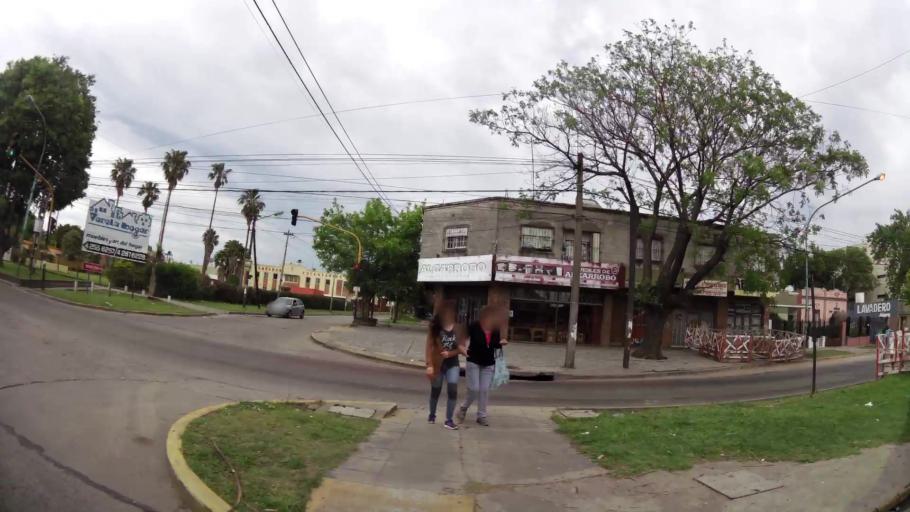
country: AR
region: Buenos Aires
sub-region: Partido de Quilmes
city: Quilmes
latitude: -34.8006
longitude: -58.2786
